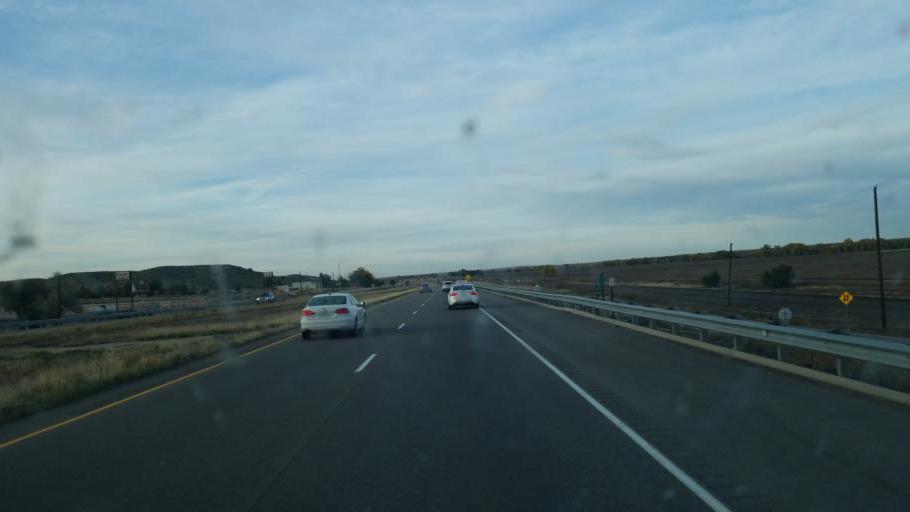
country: US
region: Colorado
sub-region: Pueblo County
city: Pueblo West
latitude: 38.4325
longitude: -104.6069
